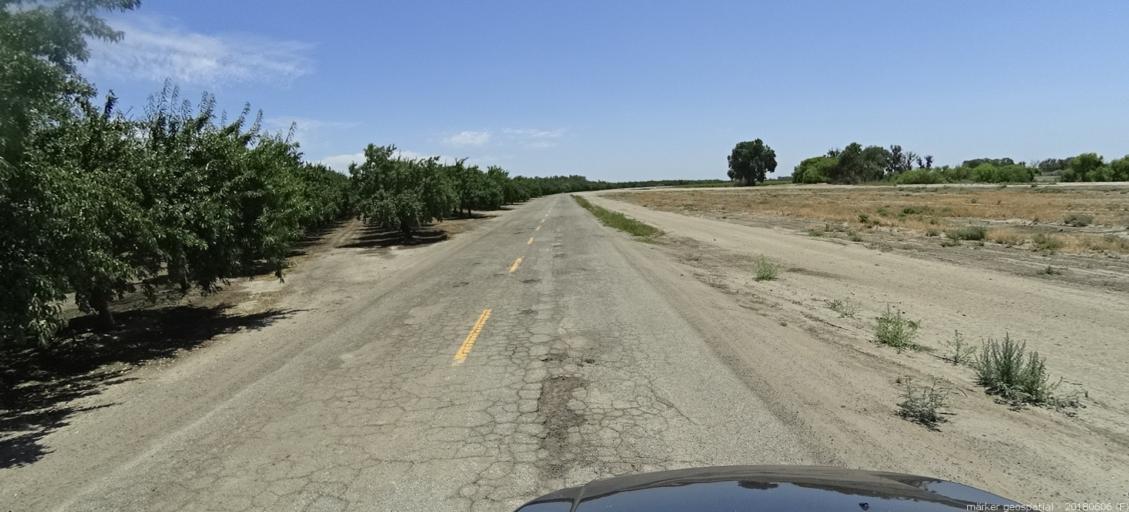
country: US
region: California
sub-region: Fresno County
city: Firebaugh
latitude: 36.8415
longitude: -120.4119
